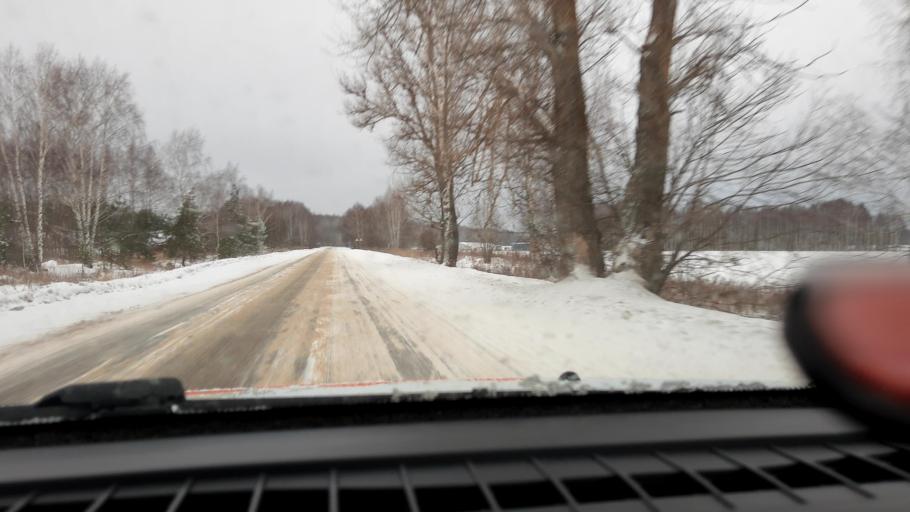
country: RU
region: Nizjnij Novgorod
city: Pamyat' Parizhskoy Kommuny
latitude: 56.2494
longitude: 44.4847
